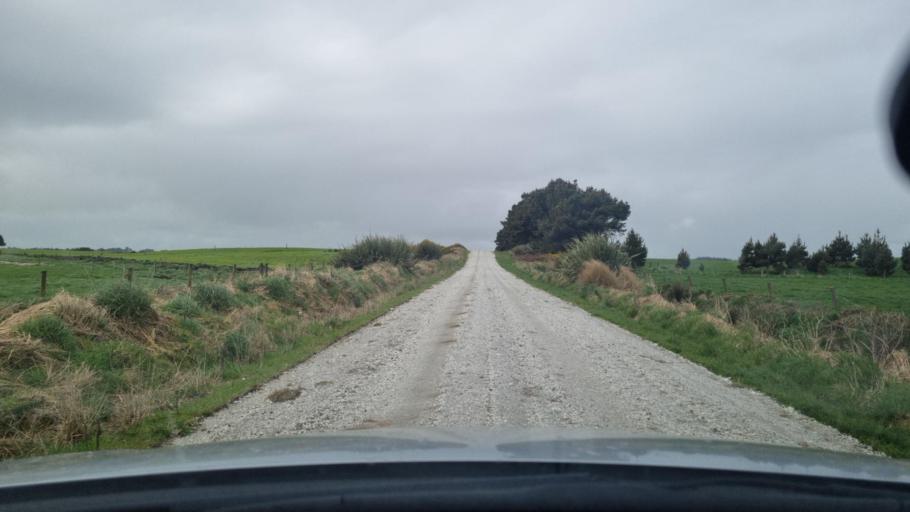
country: NZ
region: Southland
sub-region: Invercargill City
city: Invercargill
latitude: -46.5019
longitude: 168.4066
